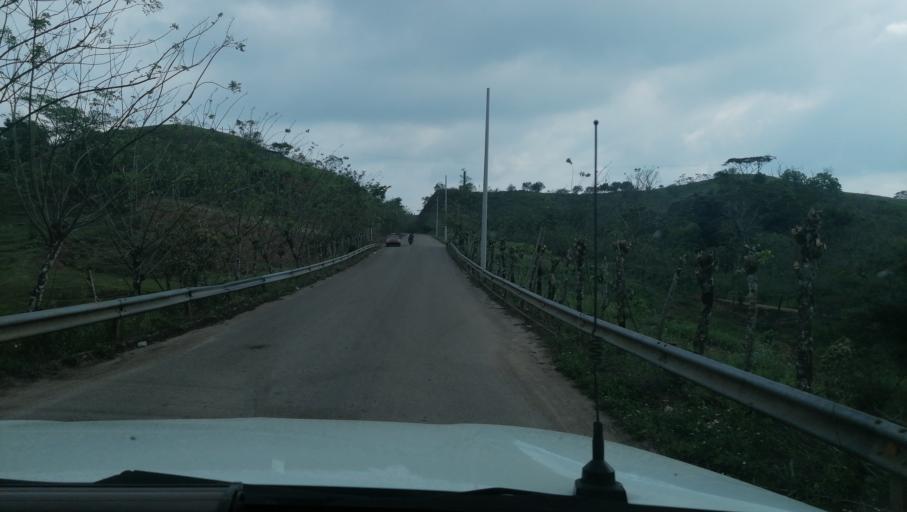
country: MX
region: Chiapas
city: Tecpatan
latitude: 17.1943
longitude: -93.3489
